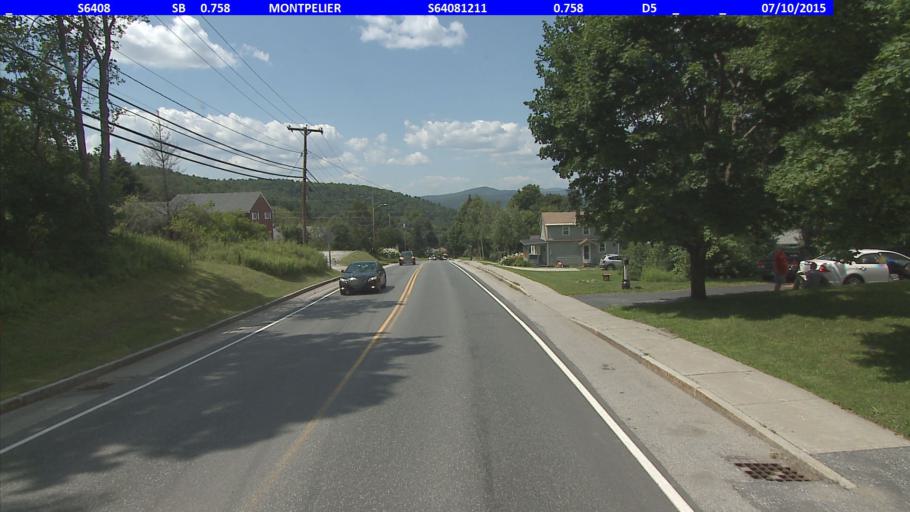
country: US
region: Vermont
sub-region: Washington County
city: Montpelier
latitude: 44.2422
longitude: -72.5638
